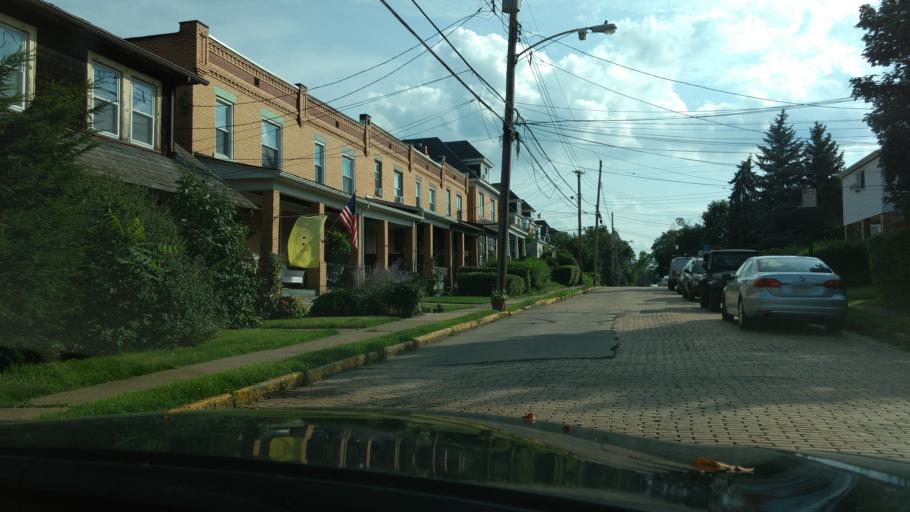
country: US
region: Pennsylvania
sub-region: Allegheny County
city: Bellevue
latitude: 40.4893
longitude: -80.0503
